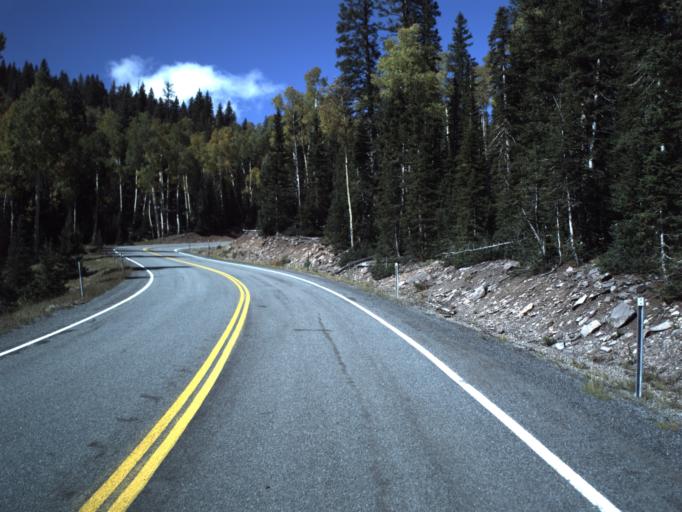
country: US
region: Utah
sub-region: Piute County
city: Junction
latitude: 38.3159
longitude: -112.3683
